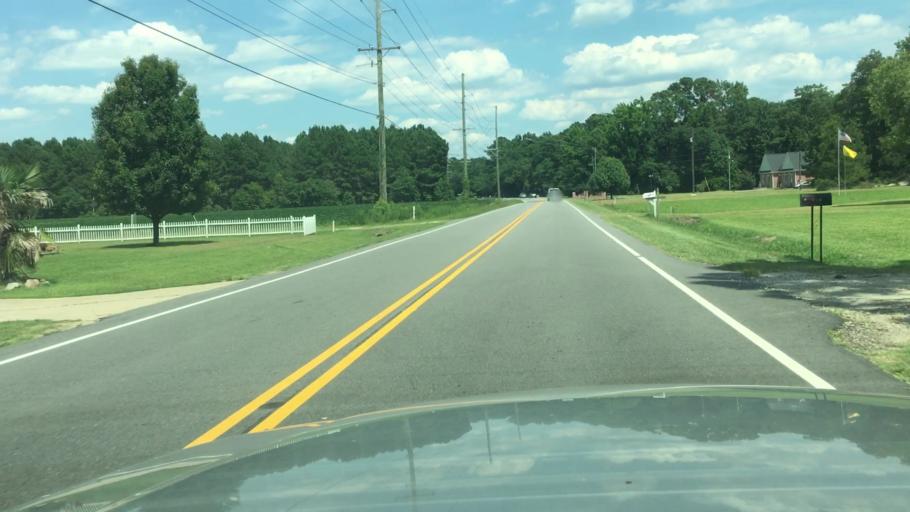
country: US
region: North Carolina
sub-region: Cumberland County
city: Hope Mills
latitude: 34.9470
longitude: -78.8697
